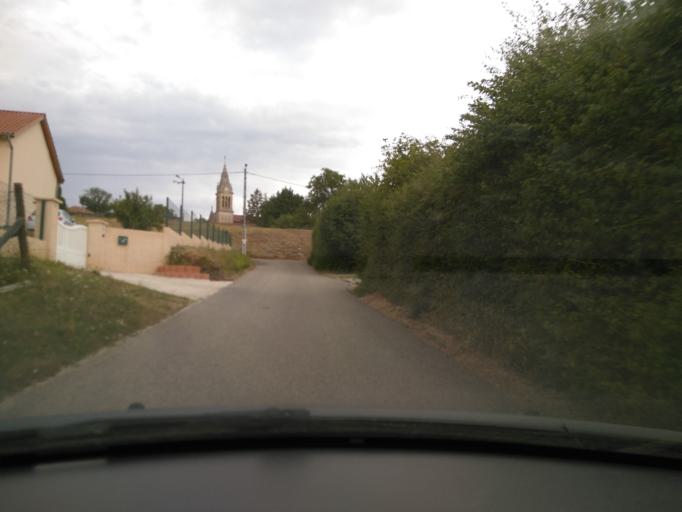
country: FR
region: Rhone-Alpes
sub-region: Departement de l'Isere
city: Beaurepaire
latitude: 45.3852
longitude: 4.9903
